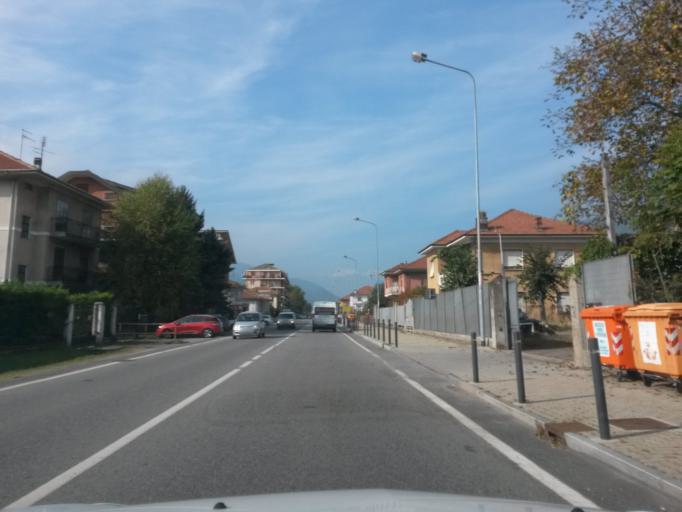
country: IT
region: Piedmont
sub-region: Provincia di Torino
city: Chiusa di San Michele
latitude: 45.1060
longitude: 7.3218
